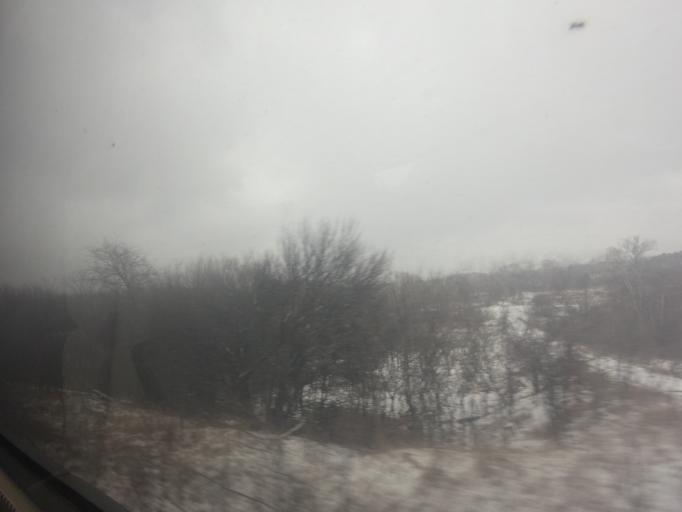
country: CA
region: Ontario
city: Cobourg
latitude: 43.9266
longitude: -78.4202
